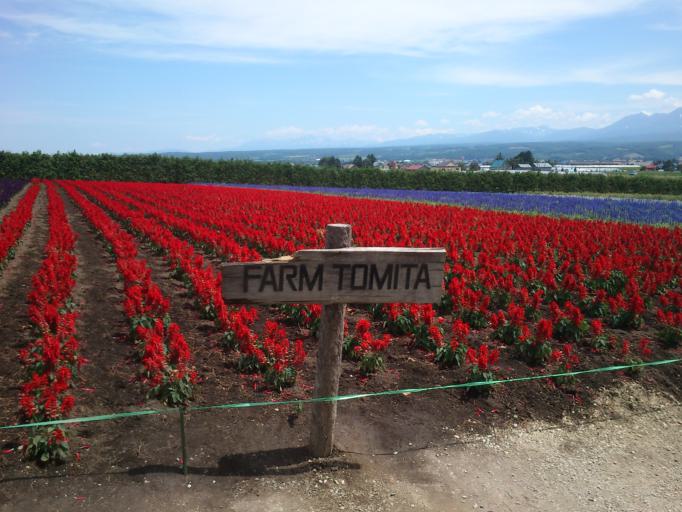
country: JP
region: Hokkaido
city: Shimo-furano
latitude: 43.4185
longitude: 142.4284
